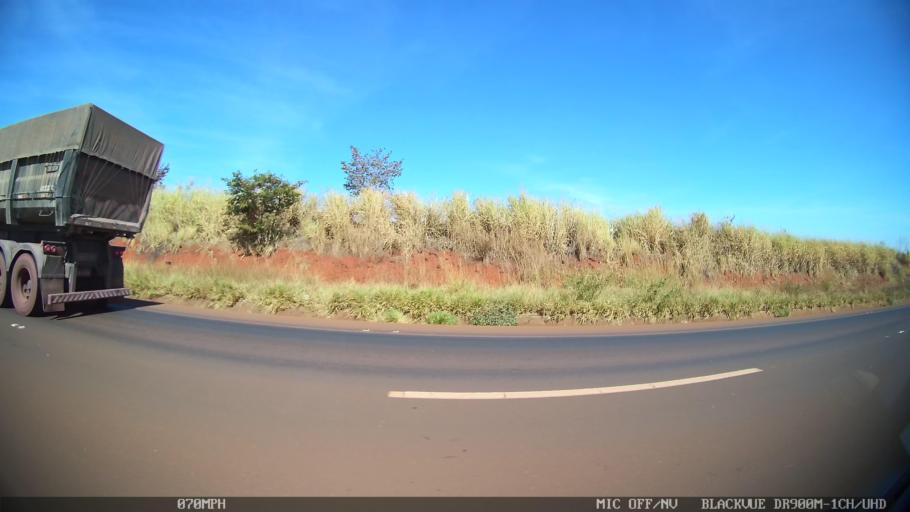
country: BR
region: Sao Paulo
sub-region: Sao Joaquim Da Barra
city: Sao Joaquim da Barra
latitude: -20.5514
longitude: -47.7396
